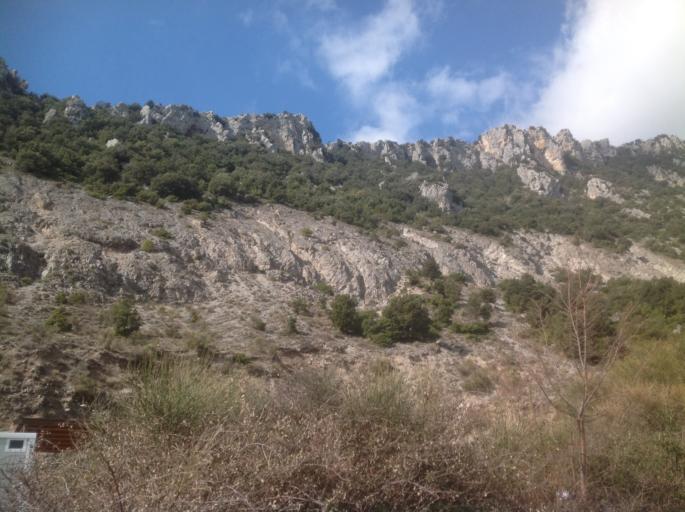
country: IT
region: Calabria
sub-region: Provincia di Cosenza
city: Civita
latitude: 39.8308
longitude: 16.3026
